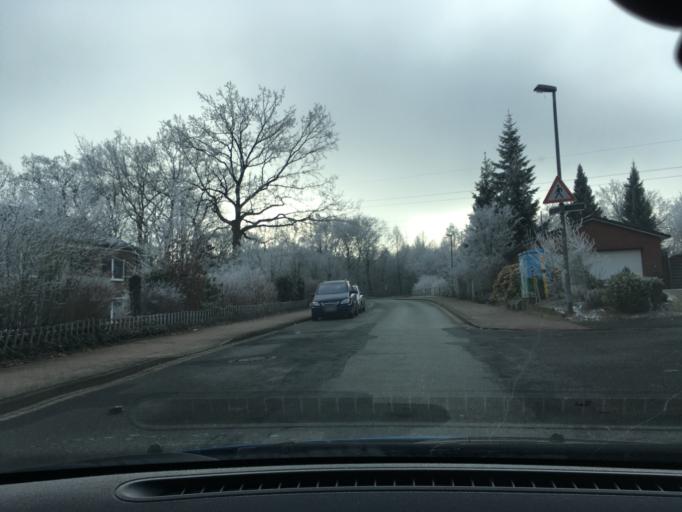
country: DE
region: Lower Saxony
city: Bardowick
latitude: 53.2734
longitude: 10.3890
